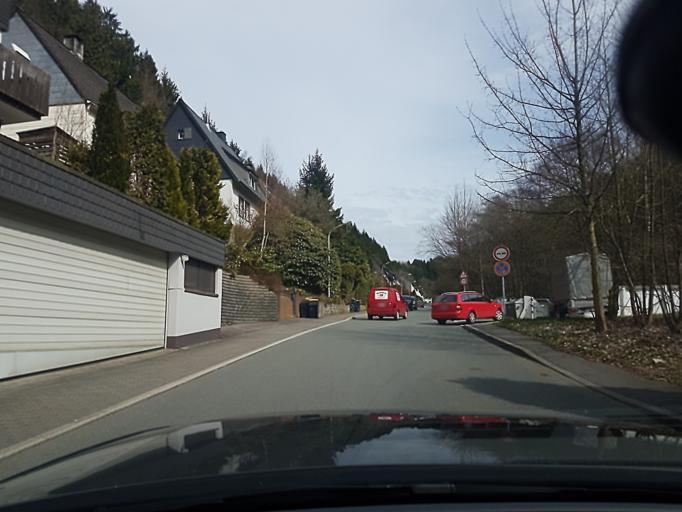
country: DE
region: North Rhine-Westphalia
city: Altena
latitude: 51.2638
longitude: 7.6765
